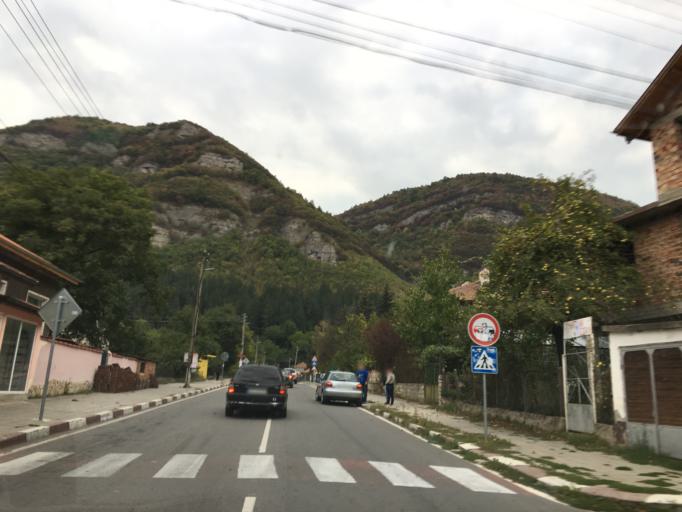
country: BG
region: Sofiya
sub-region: Obshtina Svoge
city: Svoge
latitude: 43.0041
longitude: 23.3468
